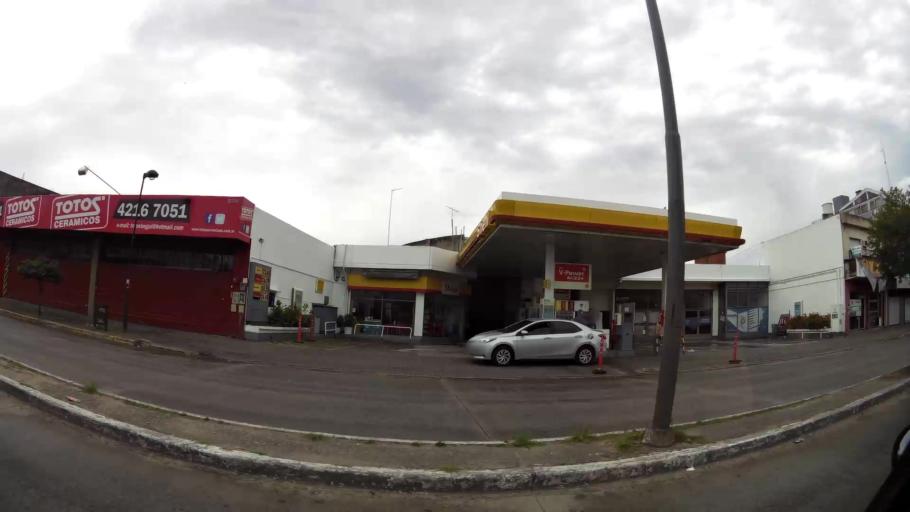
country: AR
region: Buenos Aires
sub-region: Partido de Quilmes
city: Quilmes
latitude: -34.7592
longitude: -58.2053
